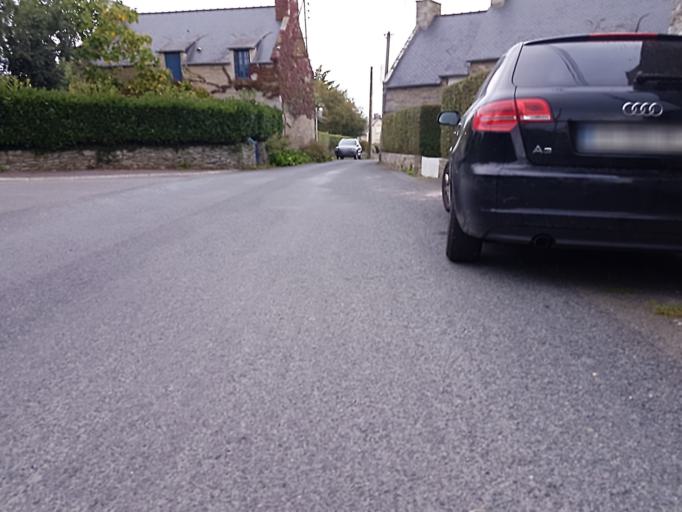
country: FR
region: Brittany
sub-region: Departement des Cotes-d'Armor
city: Saint-Cast-le-Guildo
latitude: 48.6395
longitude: -2.2594
